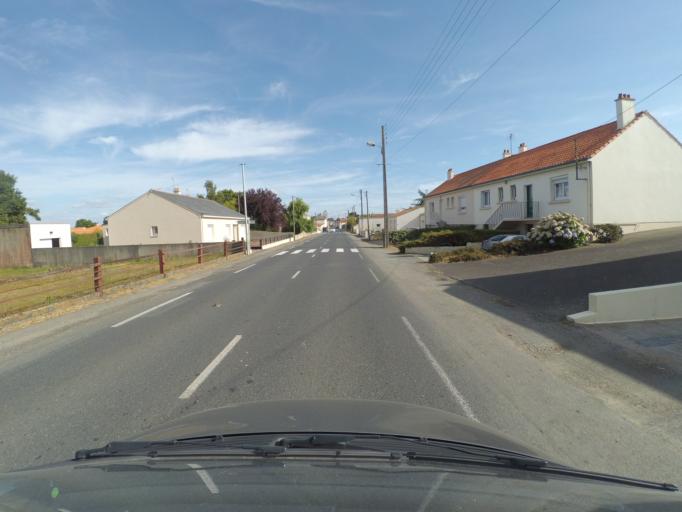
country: FR
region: Pays de la Loire
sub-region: Departement de la Loire-Atlantique
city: Vieillevigne
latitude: 46.9769
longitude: -1.4369
